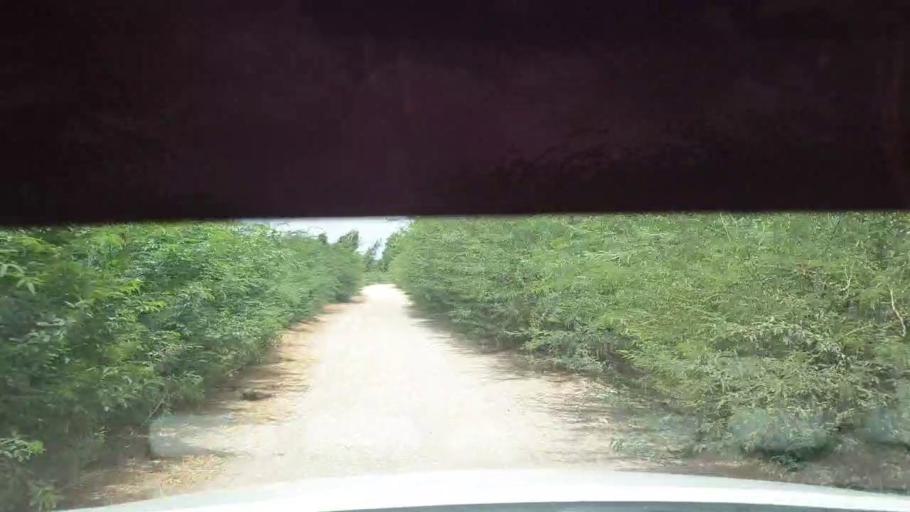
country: PK
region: Sindh
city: Kadhan
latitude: 24.4640
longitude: 69.0354
